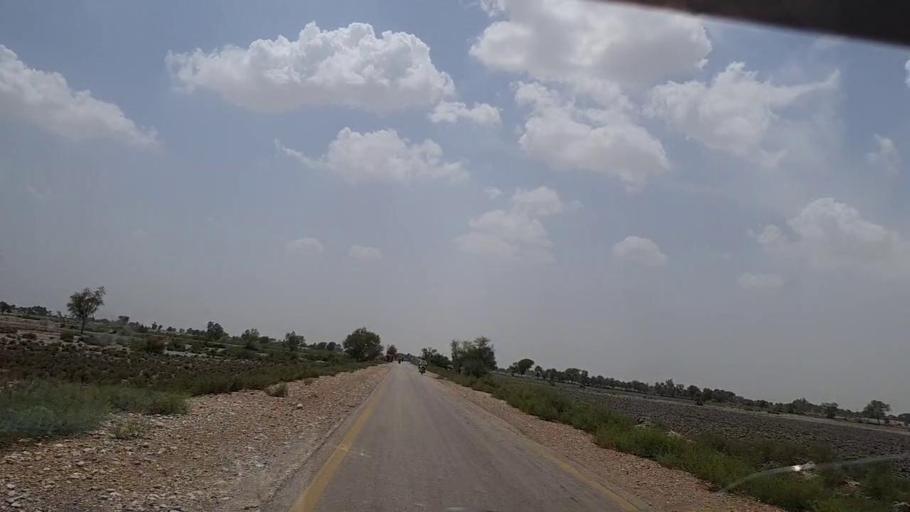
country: PK
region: Sindh
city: Bhan
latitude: 26.5416
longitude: 67.6461
